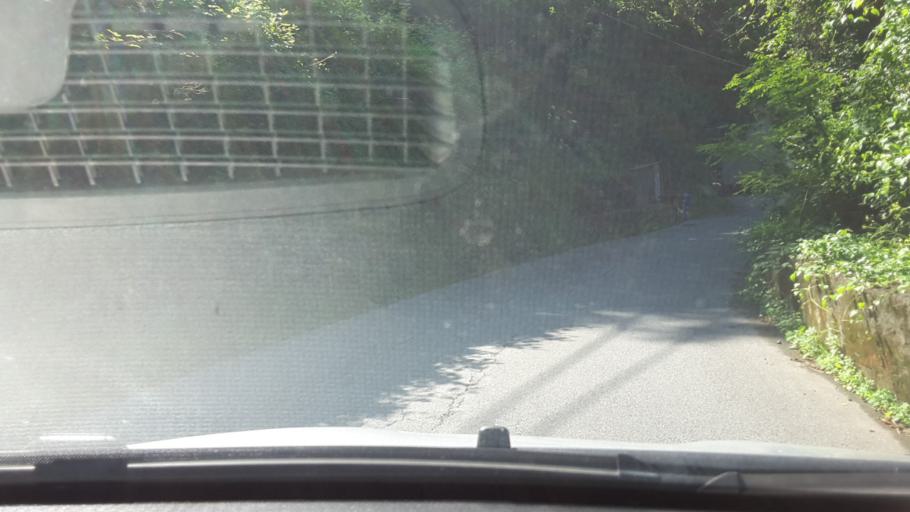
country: IT
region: Liguria
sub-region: Provincia di Genova
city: Mele
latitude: 44.4597
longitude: 8.7085
